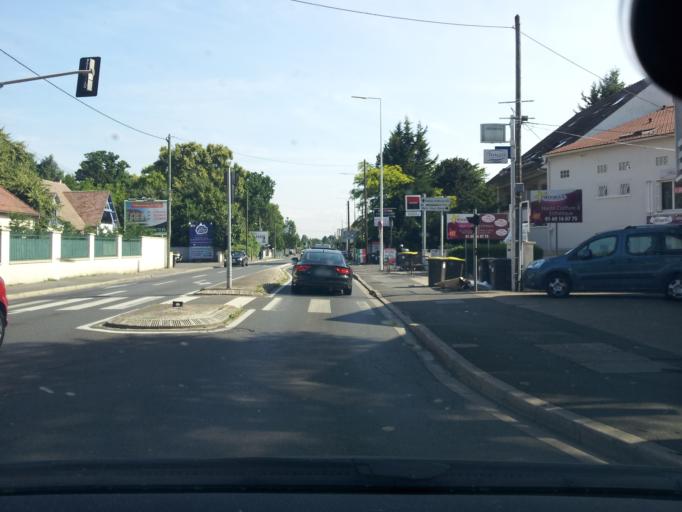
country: FR
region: Ile-de-France
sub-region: Departement de l'Essonne
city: Villemoisson-sur-Orge
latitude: 48.6571
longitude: 2.3393
